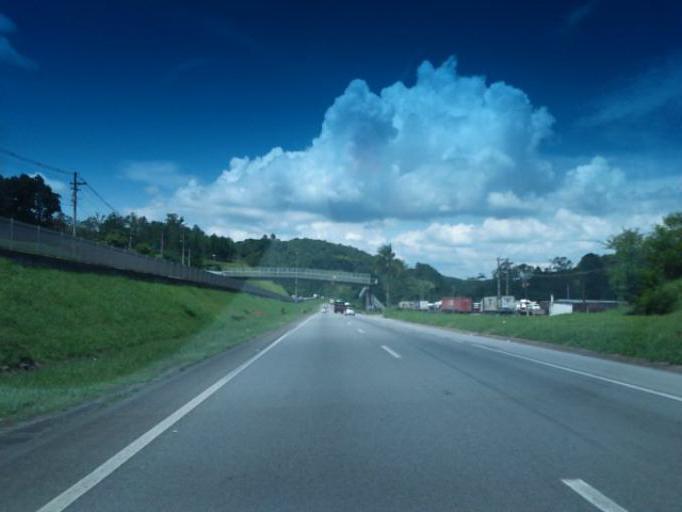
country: BR
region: Sao Paulo
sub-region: Juquitiba
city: Juquitiba
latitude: -23.9376
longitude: -47.0377
